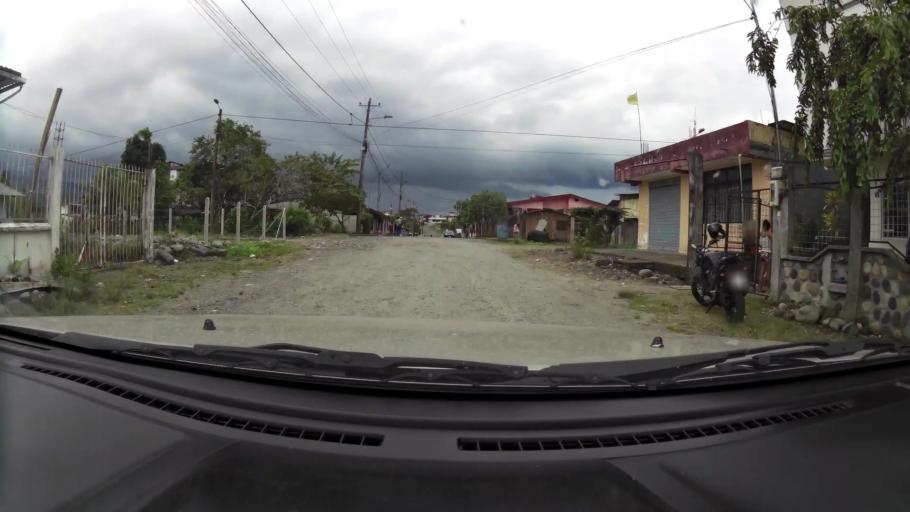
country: EC
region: Pastaza
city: Puyo
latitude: -1.4949
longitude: -78.0041
